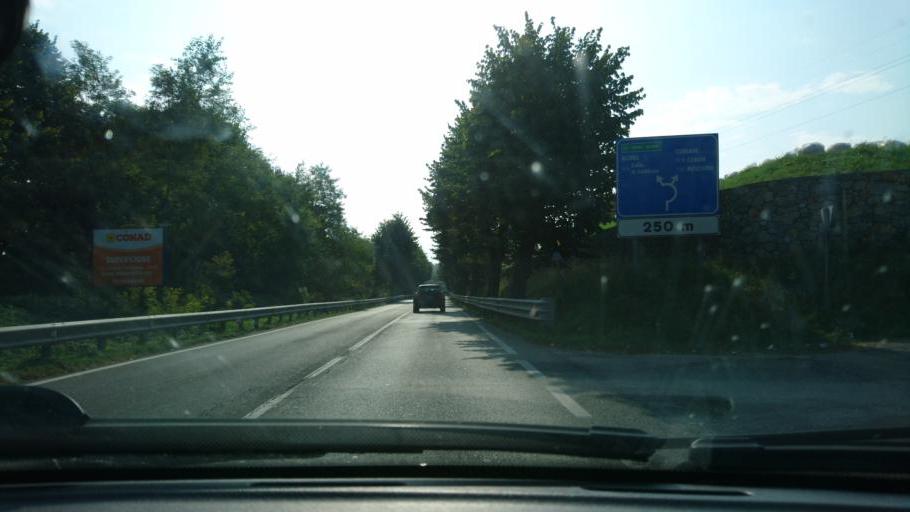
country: IT
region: Liguria
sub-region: Provincia di Savona
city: Cairo Montenotte
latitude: 44.3753
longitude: 8.2830
